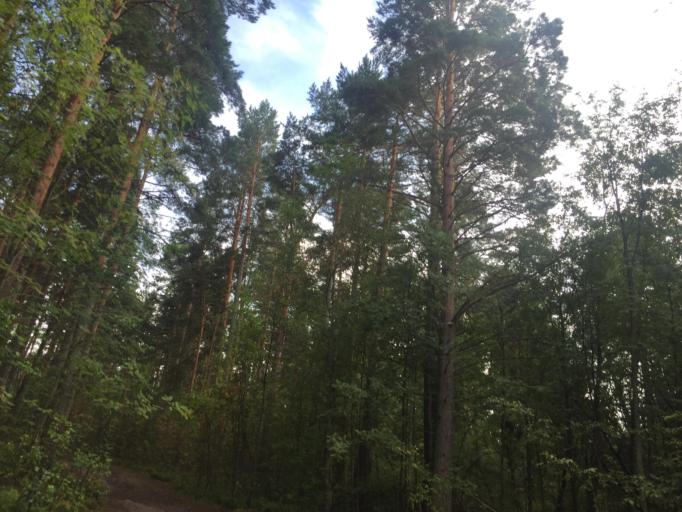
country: RU
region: Leningrad
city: Priozersk
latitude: 60.9735
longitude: 30.3024
